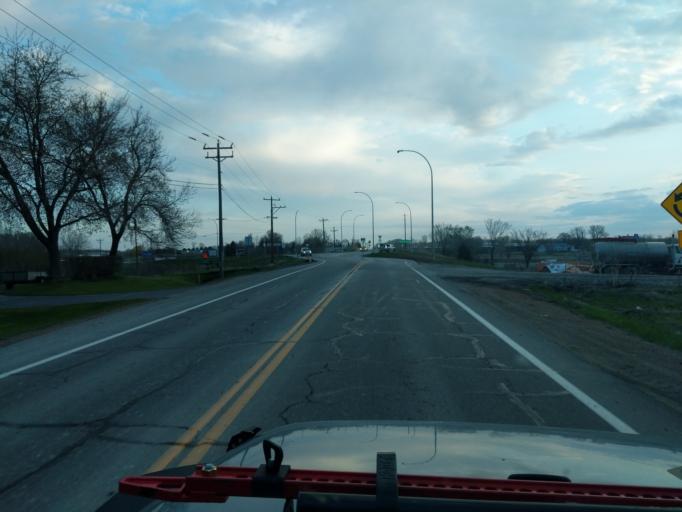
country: US
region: Minnesota
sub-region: Hennepin County
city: Rogers
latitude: 45.1614
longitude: -93.5216
